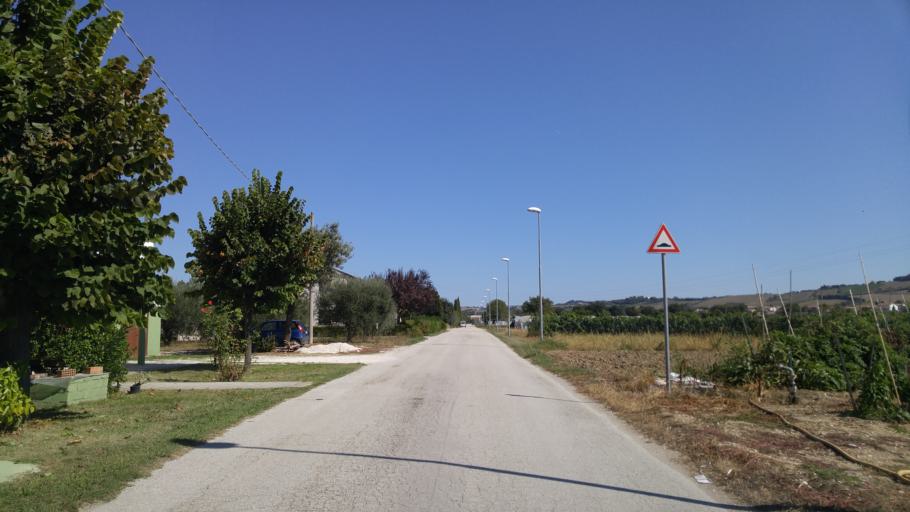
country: IT
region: The Marches
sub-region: Provincia di Pesaro e Urbino
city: Villanova
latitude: 43.7523
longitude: 12.9379
